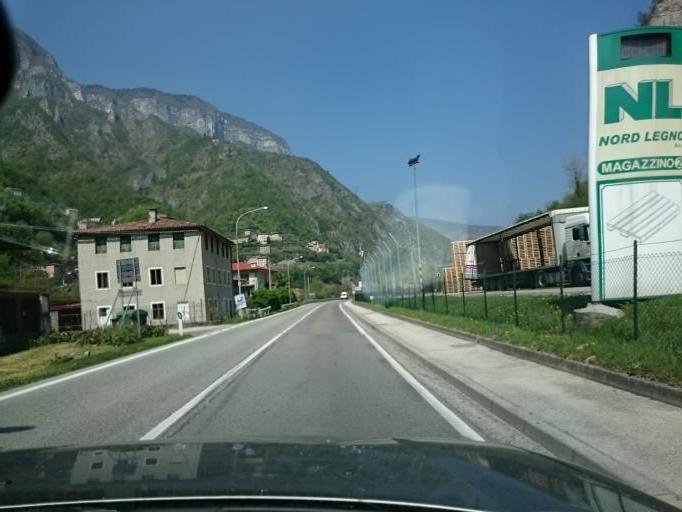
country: IT
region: Veneto
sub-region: Provincia di Vicenza
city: Valstagna
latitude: 45.8615
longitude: 11.6610
